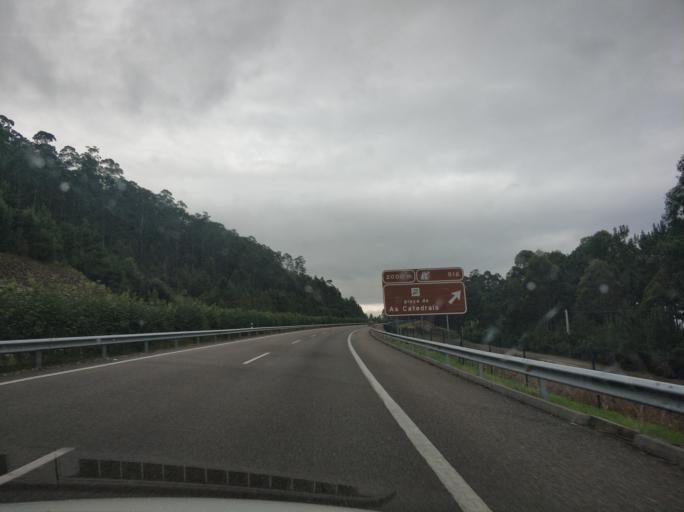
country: ES
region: Galicia
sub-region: Provincia de Lugo
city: Ribadeo
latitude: 43.5348
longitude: -7.1229
